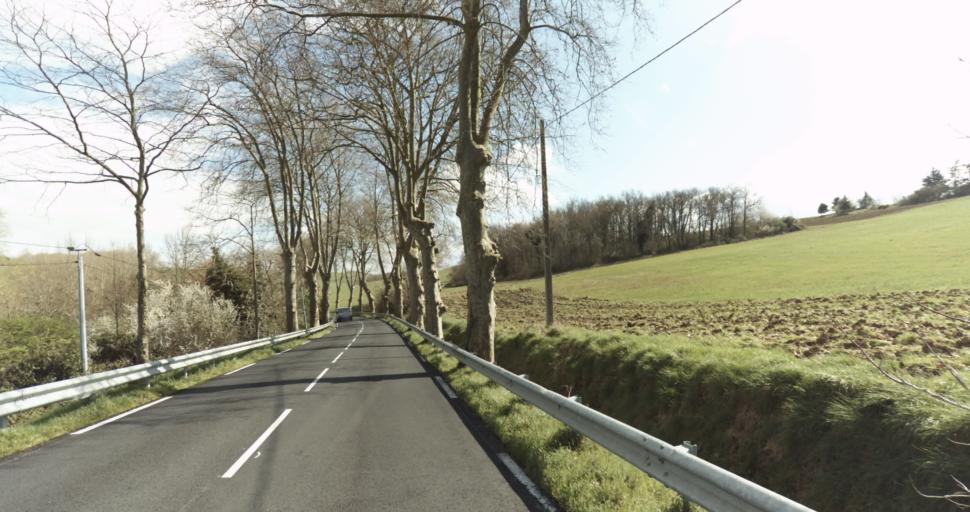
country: FR
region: Midi-Pyrenees
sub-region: Departement de la Haute-Garonne
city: Auterive
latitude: 43.3572
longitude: 1.5043
